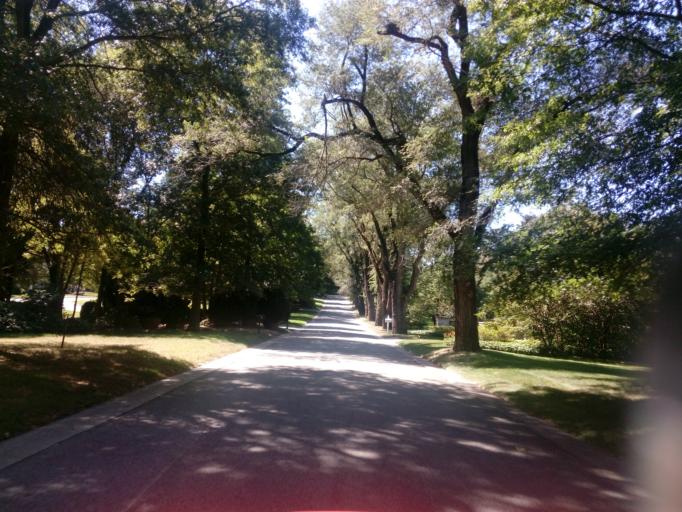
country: US
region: New York
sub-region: Nassau County
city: Old Brookville
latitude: 40.8397
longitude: -73.5863
